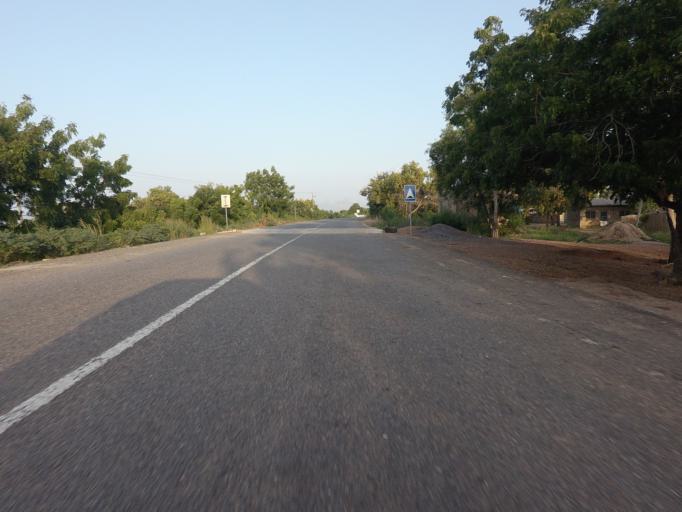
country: GH
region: Volta
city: Anloga
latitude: 5.8617
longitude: 0.7629
